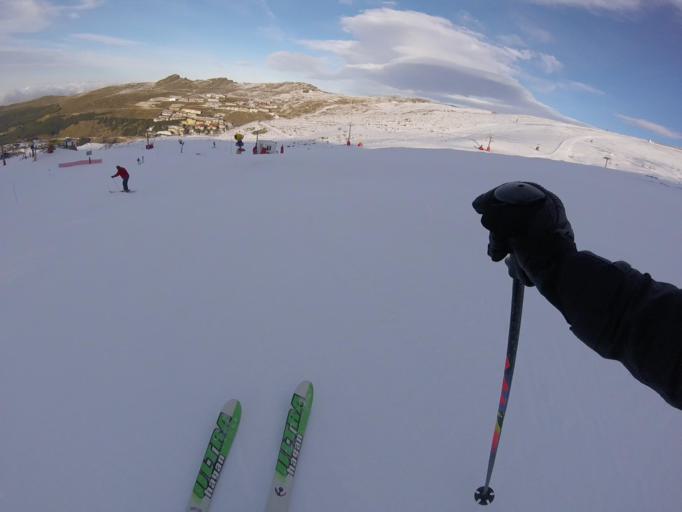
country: ES
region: Andalusia
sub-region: Provincia de Granada
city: Guejar-Sierra
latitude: 37.0796
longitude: -3.4050
